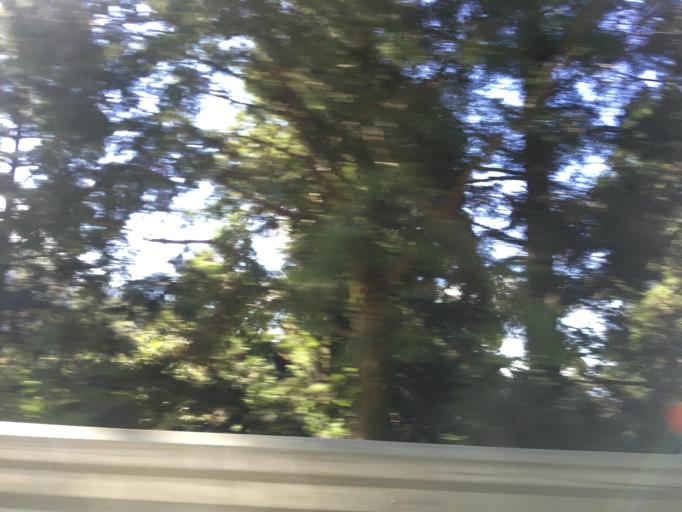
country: TW
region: Taiwan
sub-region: Yilan
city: Yilan
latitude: 24.5135
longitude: 121.5703
